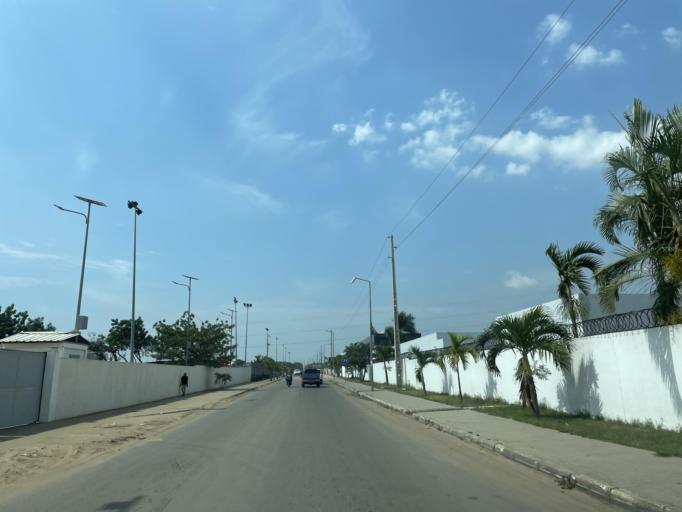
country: AO
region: Luanda
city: Luanda
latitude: -8.9768
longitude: 13.3392
